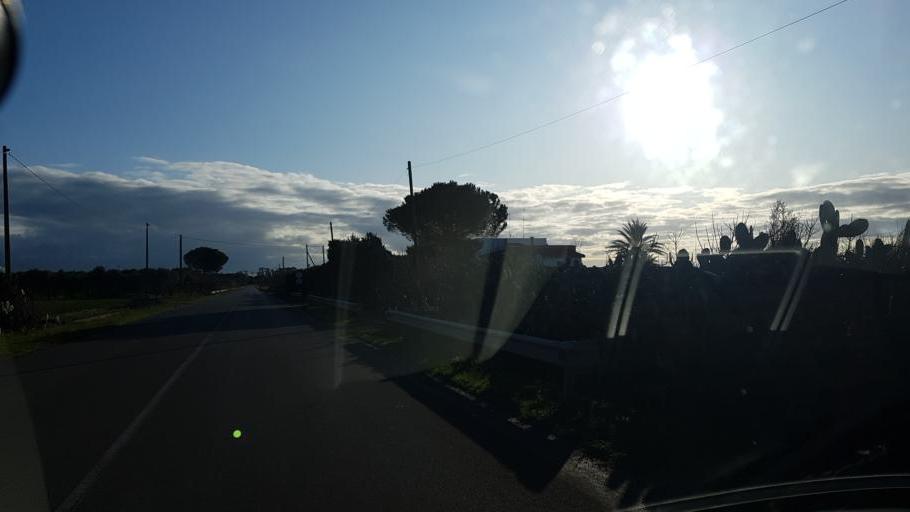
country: IT
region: Apulia
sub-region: Provincia di Brindisi
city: Tuturano
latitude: 40.5604
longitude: 18.0131
